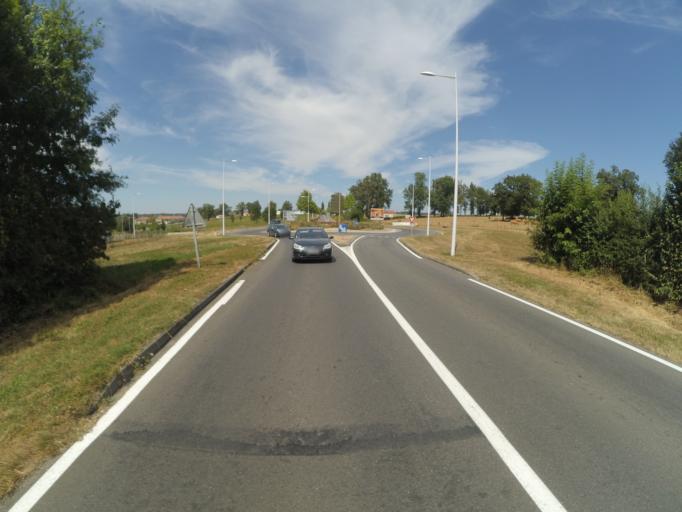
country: FR
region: Poitou-Charentes
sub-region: Departement de la Charente
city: Confolens
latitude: 45.9990
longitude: 0.6733
